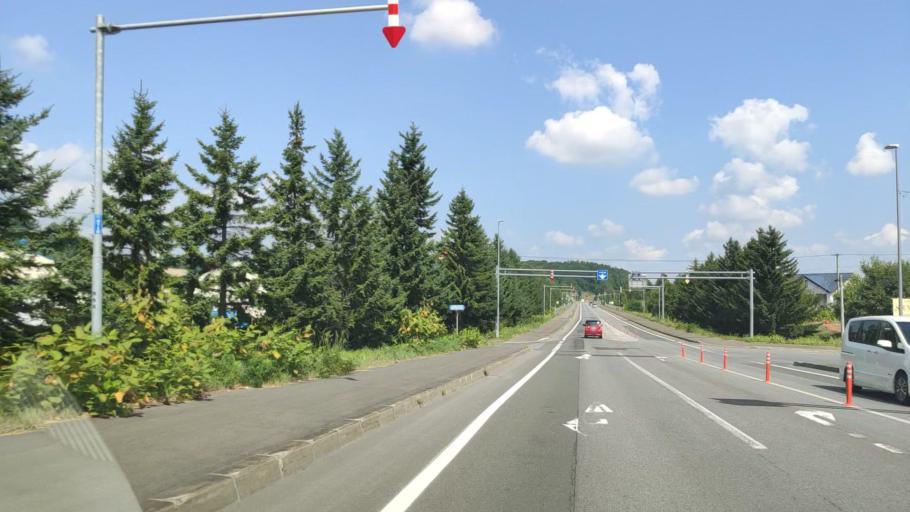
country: JP
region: Hokkaido
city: Shimo-furano
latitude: 43.4652
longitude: 142.4559
